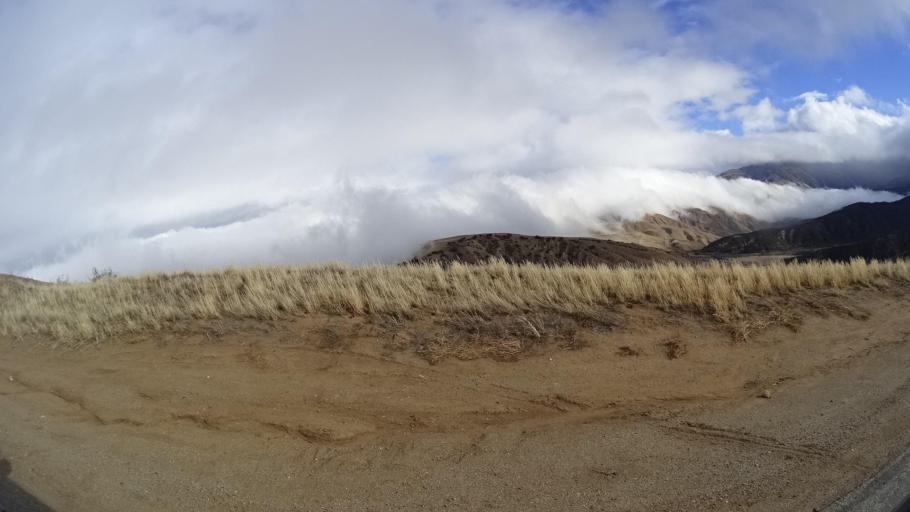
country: US
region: California
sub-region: Kern County
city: Maricopa
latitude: 34.8936
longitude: -119.3618
